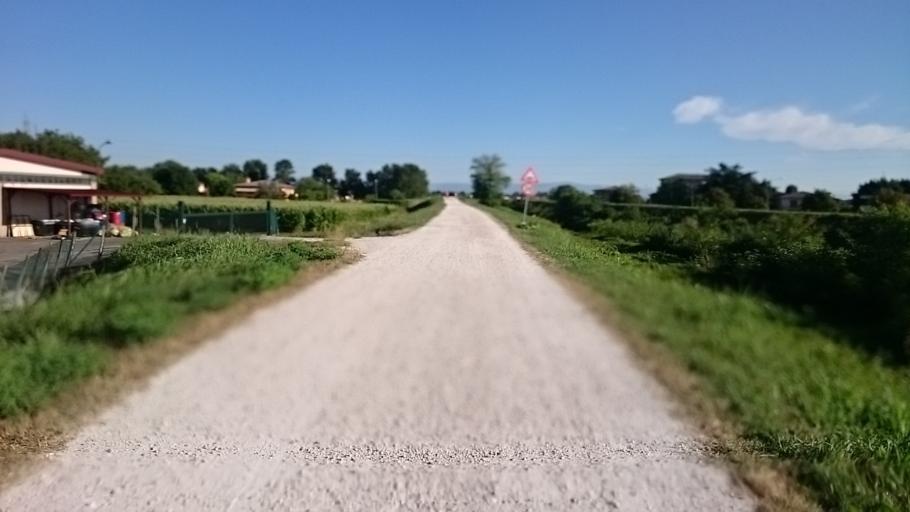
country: IT
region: Veneto
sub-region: Provincia di Padova
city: Vigodarzere
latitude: 45.4581
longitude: 11.8958
